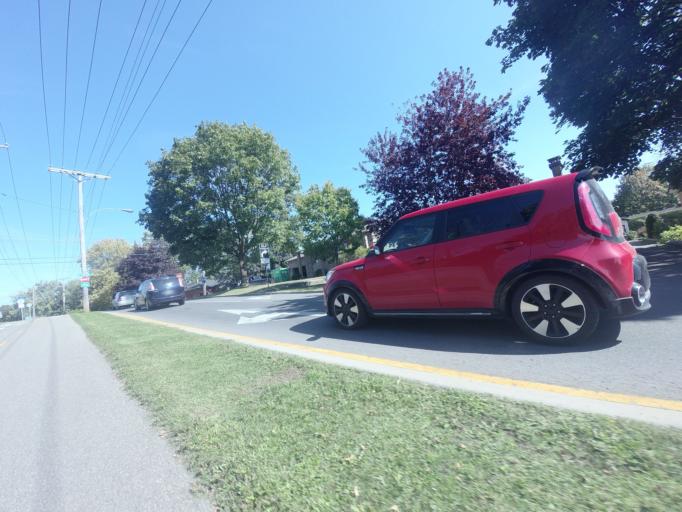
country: CA
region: Quebec
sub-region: Laurentides
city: Saint-Eustache
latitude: 45.5606
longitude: -73.9126
